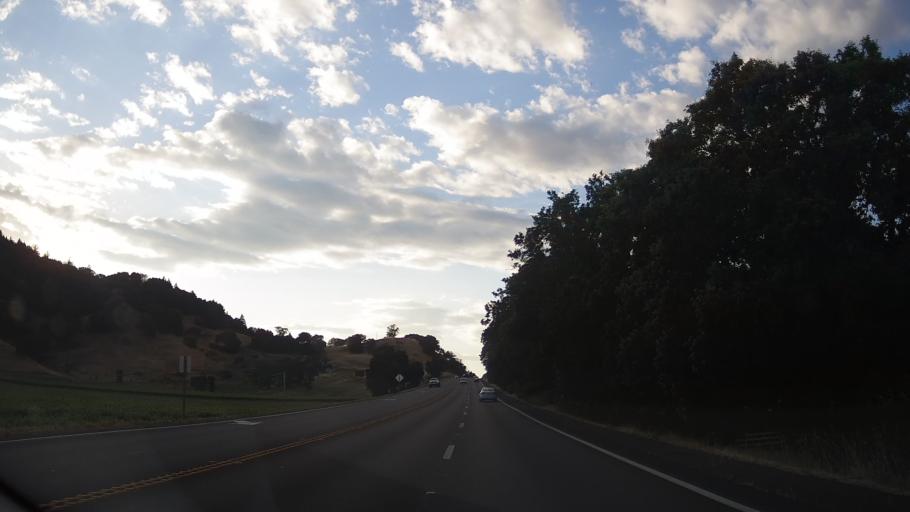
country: US
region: California
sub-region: Mendocino County
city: Talmage
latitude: 39.0233
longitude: -123.1352
